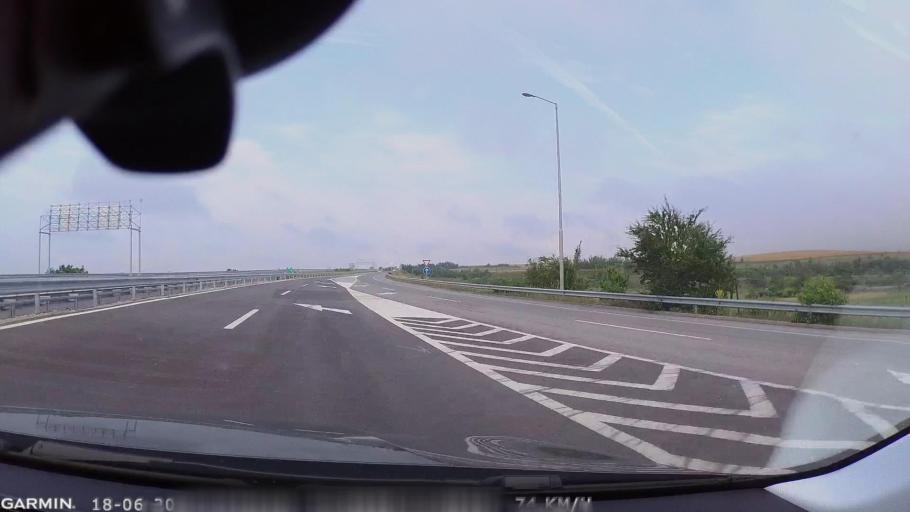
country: MK
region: Petrovec
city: Sredno Konjare
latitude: 41.9525
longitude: 21.7558
